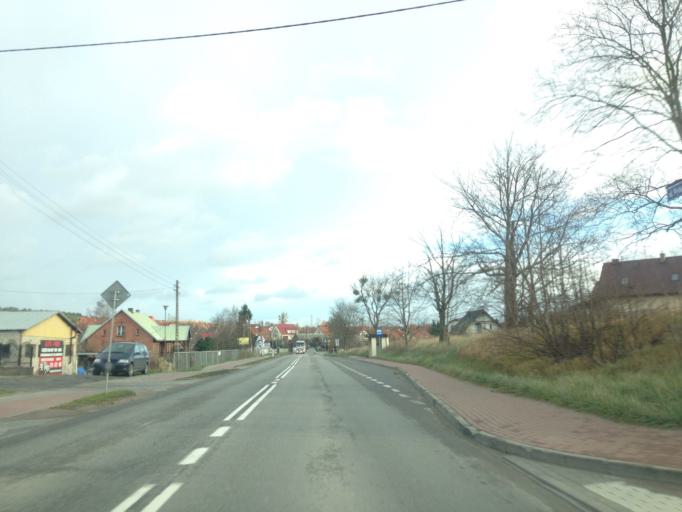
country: PL
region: Pomeranian Voivodeship
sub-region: Powiat gdanski
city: Lublewo Gdanskie
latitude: 54.2819
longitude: 18.4898
